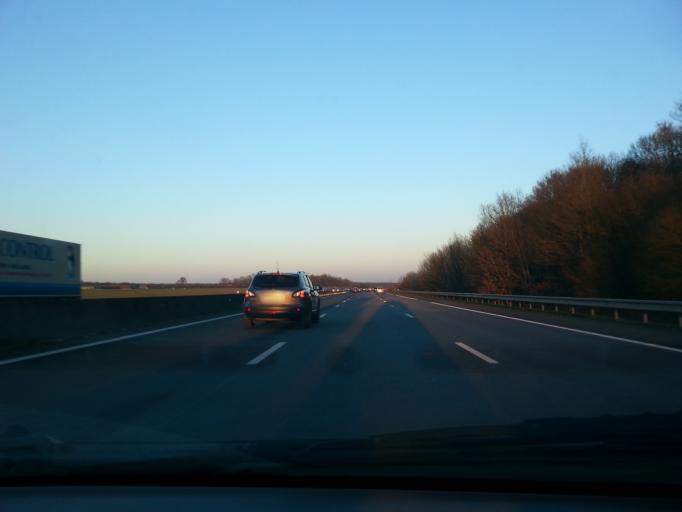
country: FR
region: Centre
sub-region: Departement d'Eure-et-Loir
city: Brou
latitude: 48.2564
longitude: 1.1310
